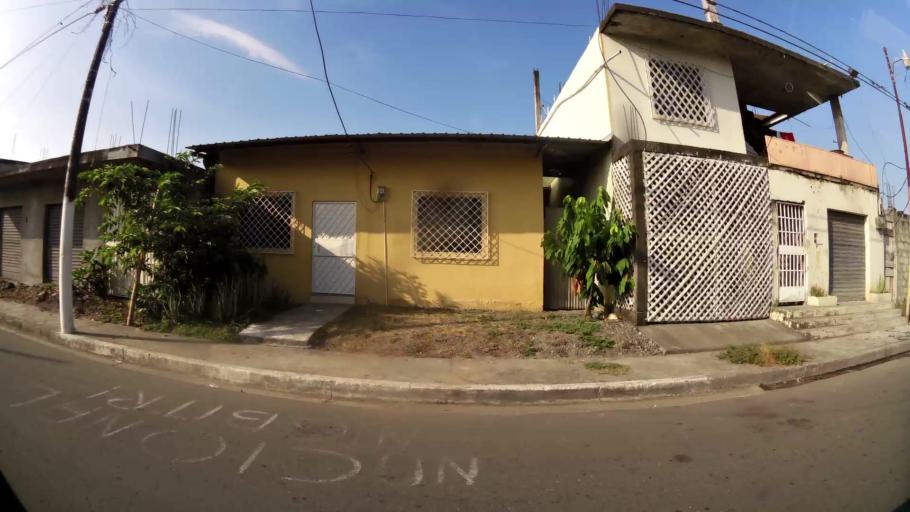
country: EC
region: Guayas
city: Eloy Alfaro
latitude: -2.1821
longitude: -79.8427
